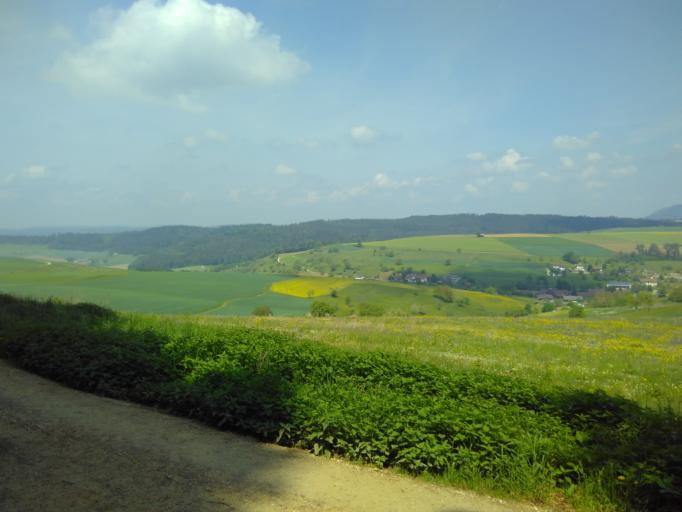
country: CH
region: Schaffhausen
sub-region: Bezirk Schleitheim
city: Schleitheim
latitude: 47.7580
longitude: 8.5354
